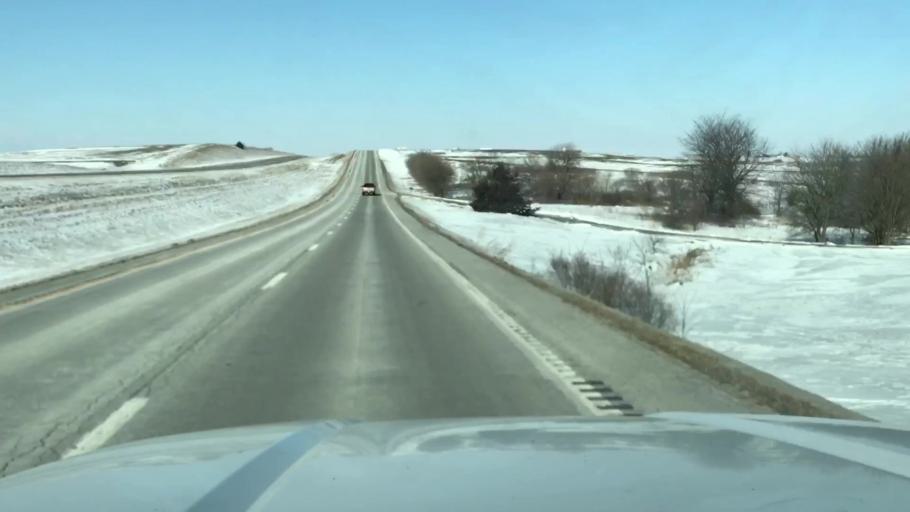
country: US
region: Missouri
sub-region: Andrew County
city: Savannah
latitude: 39.9697
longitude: -94.8702
